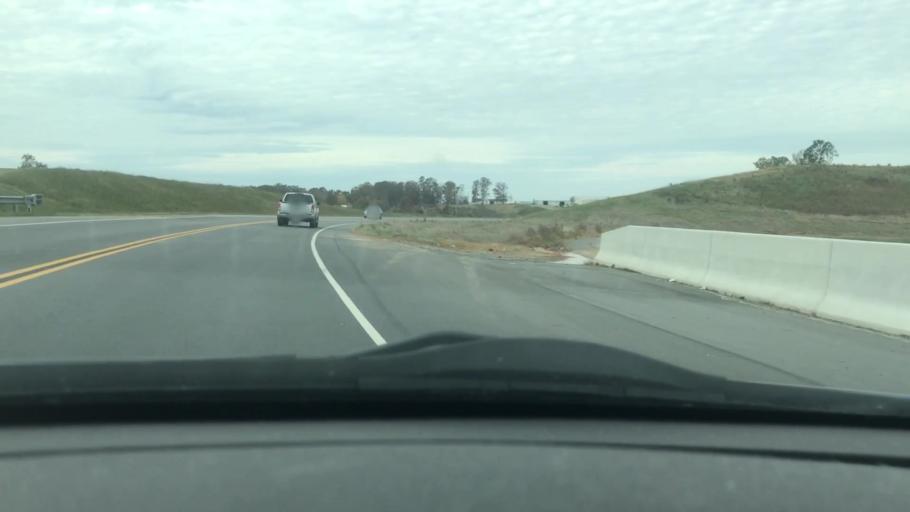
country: US
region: North Carolina
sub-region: Randolph County
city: Asheboro
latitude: 35.6977
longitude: -79.8698
